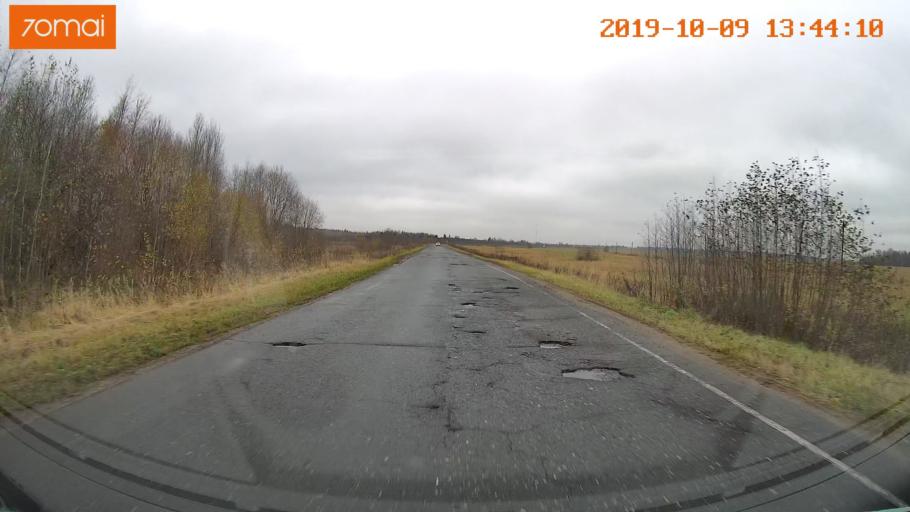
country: RU
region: Kostroma
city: Buy
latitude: 58.3646
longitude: 41.2068
